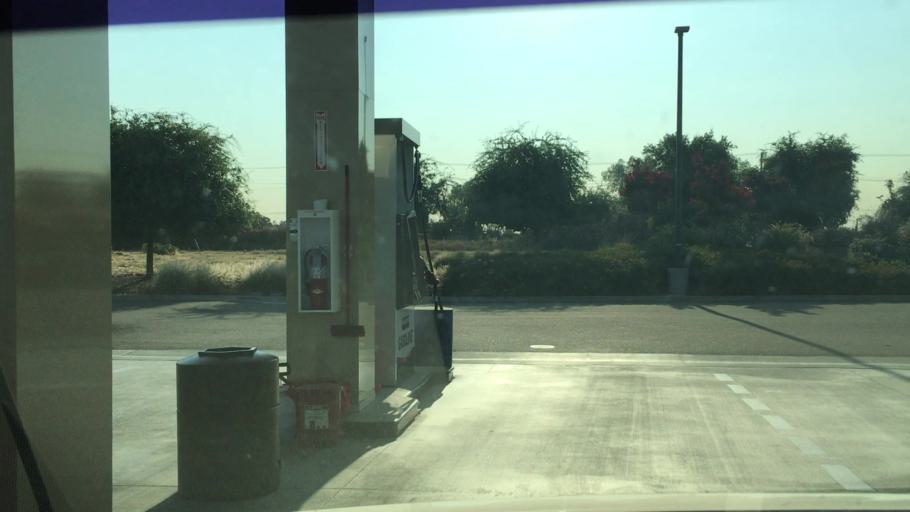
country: US
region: California
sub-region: San Joaquin County
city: Lodi
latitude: 38.0999
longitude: -121.2616
